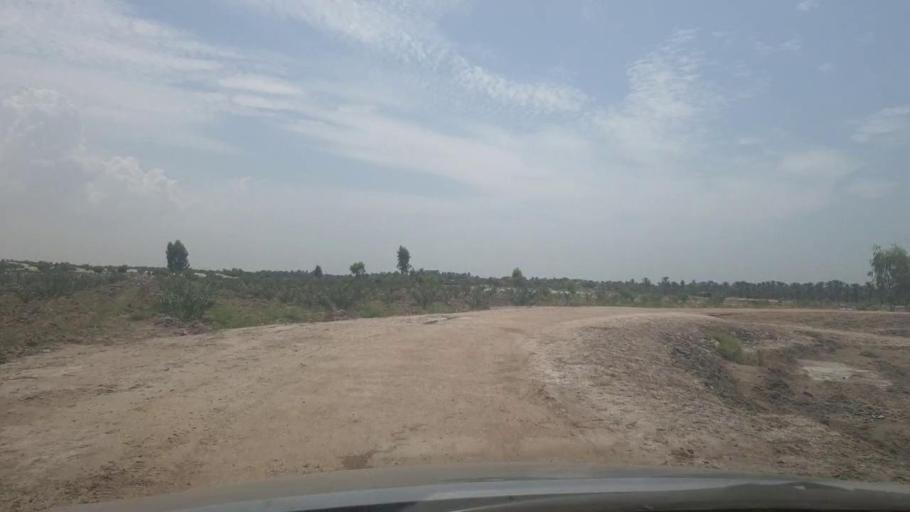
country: PK
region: Sindh
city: Kot Diji
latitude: 27.3851
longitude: 68.6981
